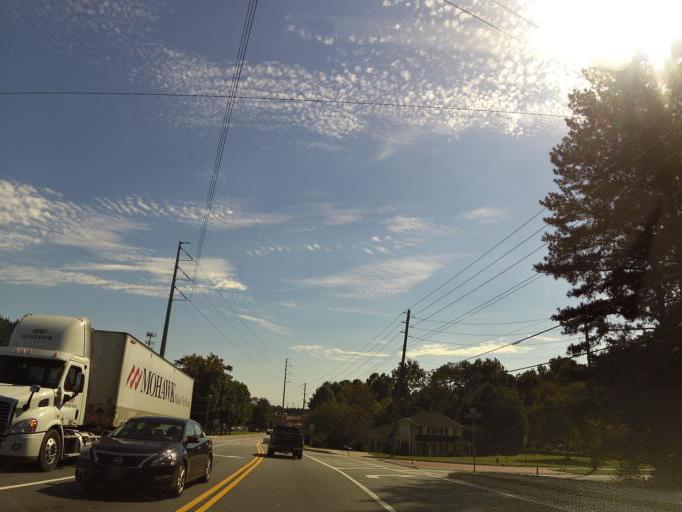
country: US
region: Georgia
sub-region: Cobb County
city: Kennesaw
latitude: 34.0510
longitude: -84.5948
